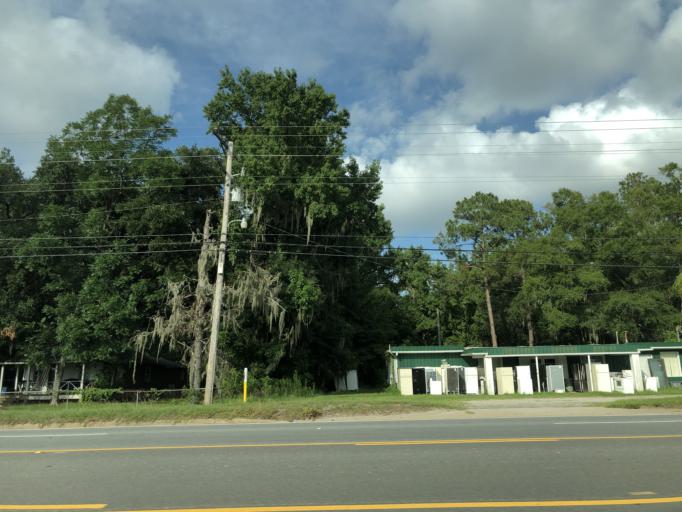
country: US
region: Georgia
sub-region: Glynn County
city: Dock Junction
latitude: 31.2640
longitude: -81.5595
